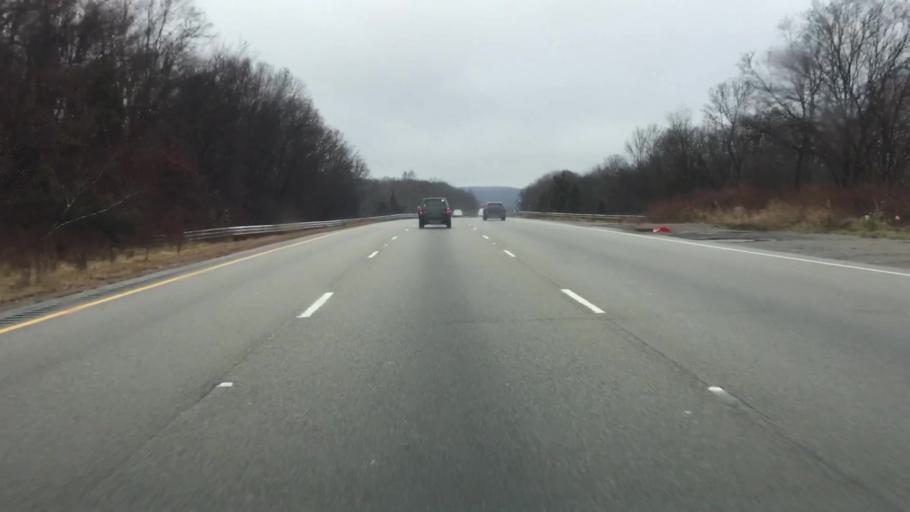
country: US
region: Massachusetts
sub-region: Worcester County
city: Southborough
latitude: 42.2938
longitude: -71.5661
